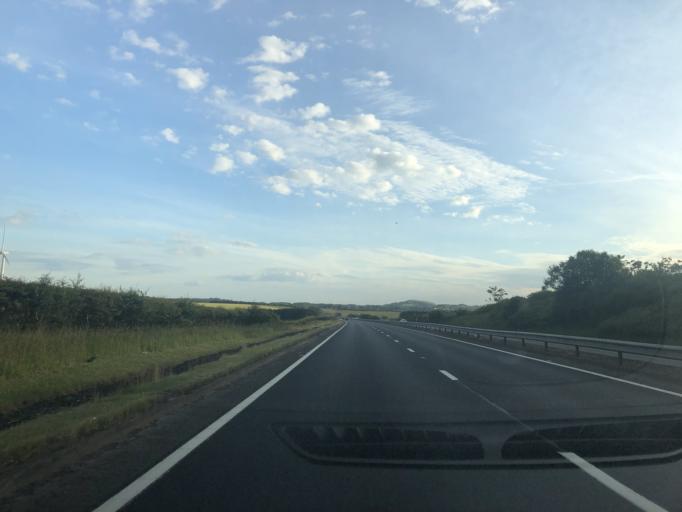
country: GB
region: Scotland
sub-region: Fife
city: Lochgelly
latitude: 56.1168
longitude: -3.3098
